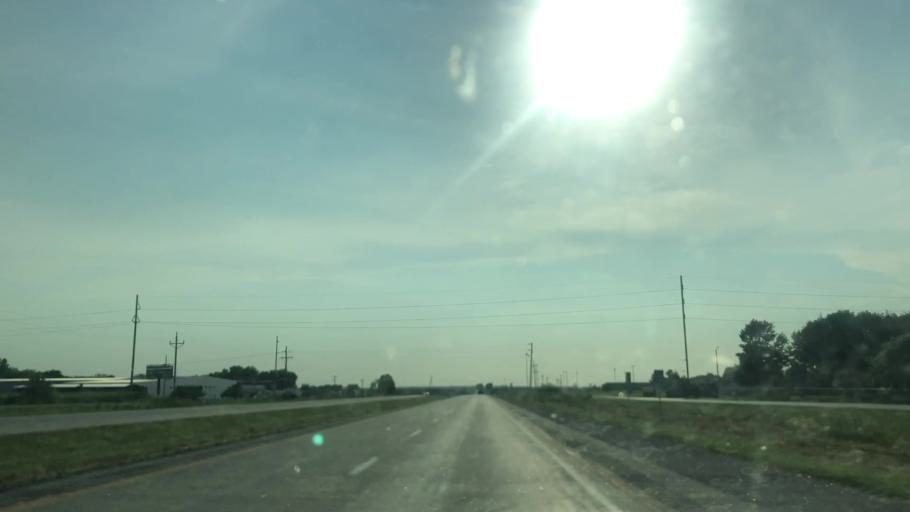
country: US
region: Iowa
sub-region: Story County
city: Ames
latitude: 42.0086
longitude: -93.5583
